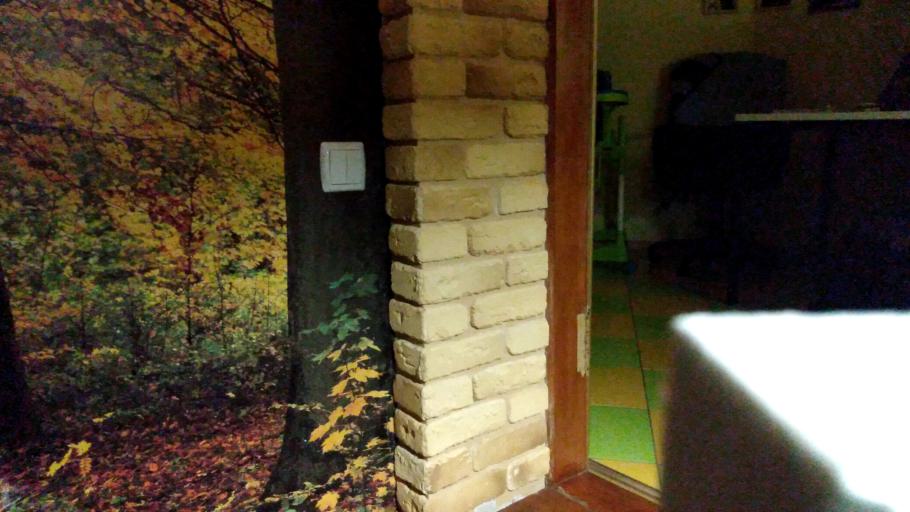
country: RU
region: Vologda
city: Lipin Bor
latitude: 60.8091
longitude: 38.0298
